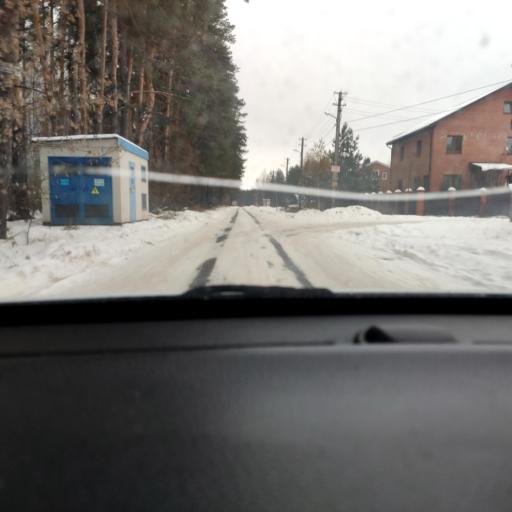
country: RU
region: Voronezj
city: Somovo
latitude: 51.7103
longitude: 39.3179
